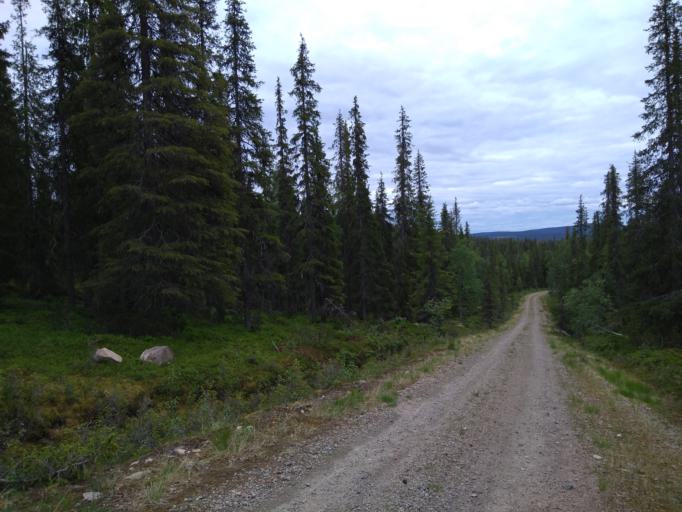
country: FI
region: Lapland
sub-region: Tunturi-Lappi
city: Muonio
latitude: 67.9653
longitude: 24.0788
